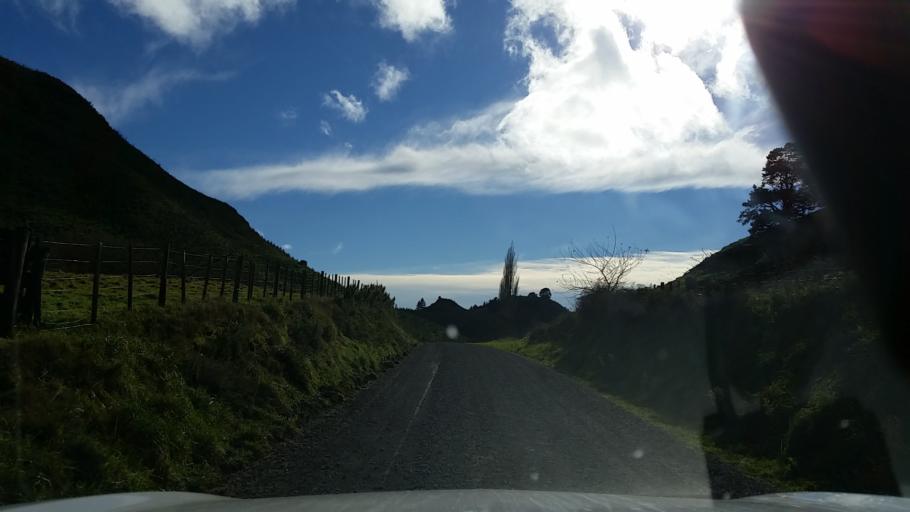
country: NZ
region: Bay of Plenty
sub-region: Rotorua District
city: Rotorua
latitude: -38.3651
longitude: 176.2078
